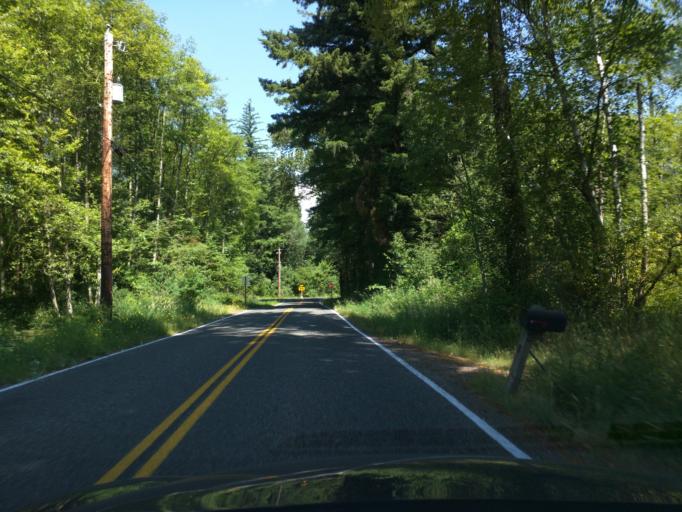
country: CA
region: British Columbia
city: Langley
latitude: 48.9924
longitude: -122.5959
